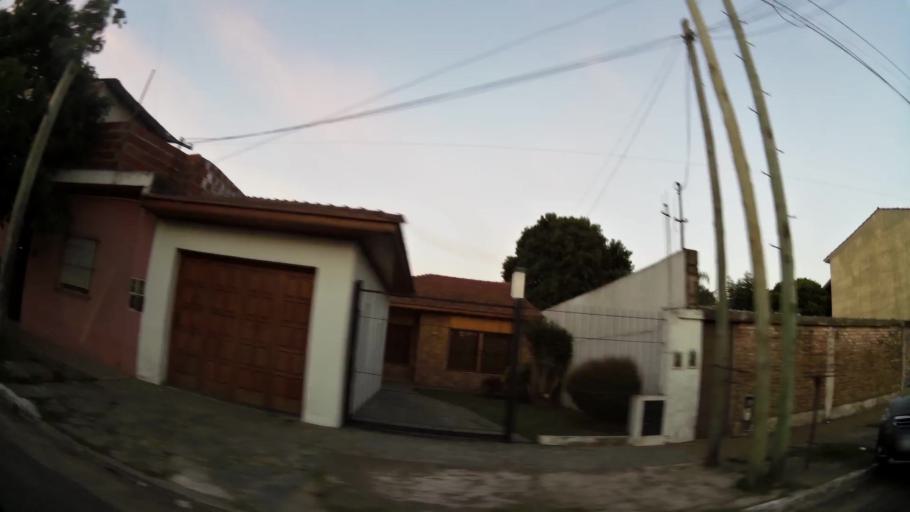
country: AR
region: Buenos Aires
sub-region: Partido de Quilmes
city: Quilmes
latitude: -34.7708
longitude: -58.2019
